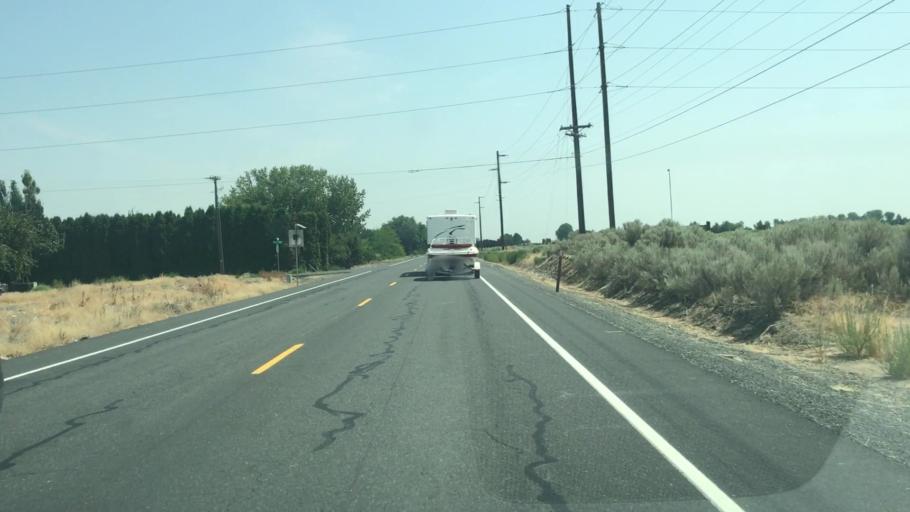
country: US
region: Washington
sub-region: Grant County
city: Quincy
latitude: 47.1613
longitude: -119.8653
